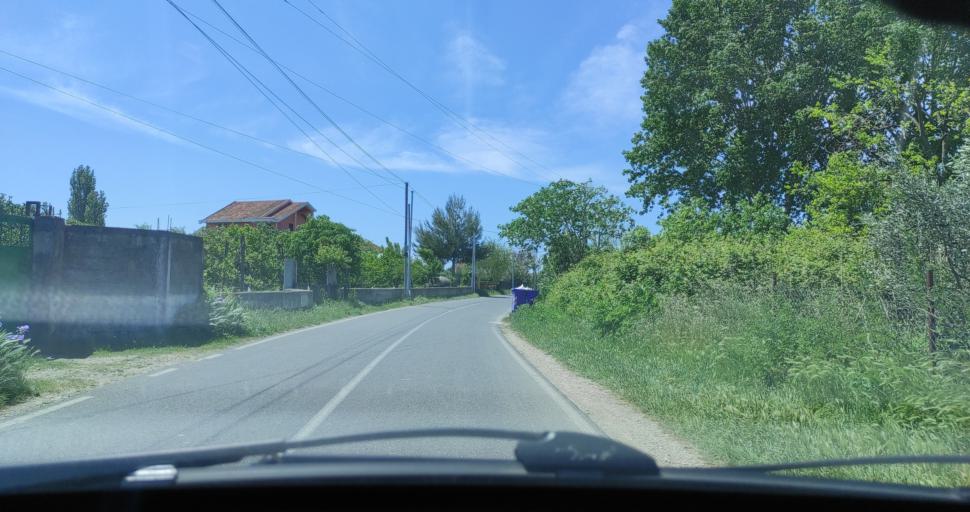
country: AL
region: Lezhe
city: Lezhe
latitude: 41.7599
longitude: 19.6289
